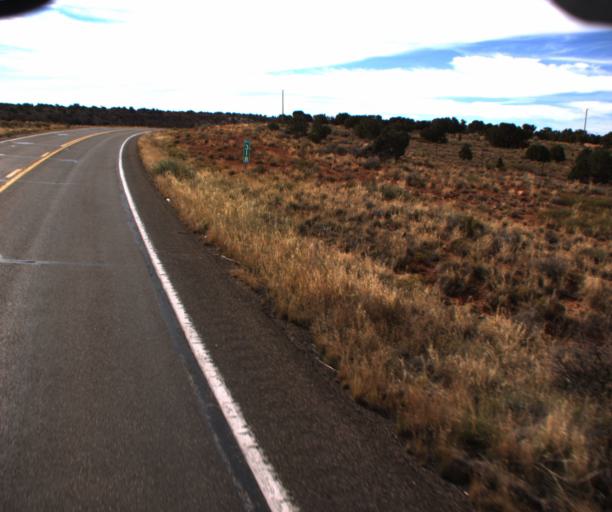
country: US
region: Arizona
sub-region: Coconino County
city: Kaibito
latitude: 36.6826
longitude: -111.2549
